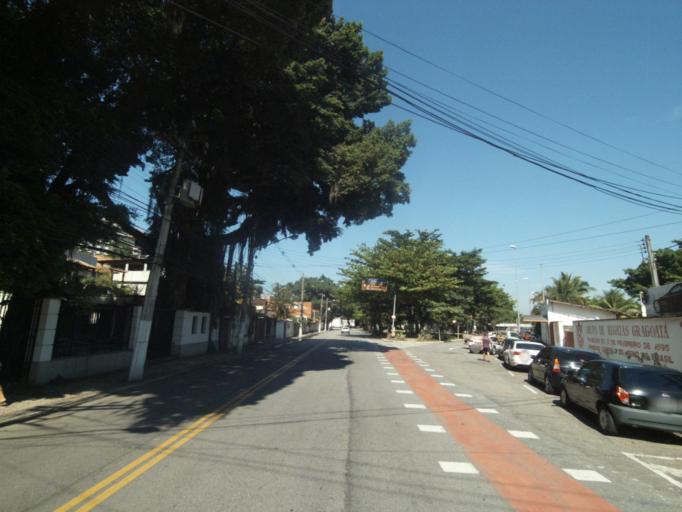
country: BR
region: Rio de Janeiro
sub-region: Niteroi
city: Niteroi
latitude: -22.9016
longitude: -43.1336
